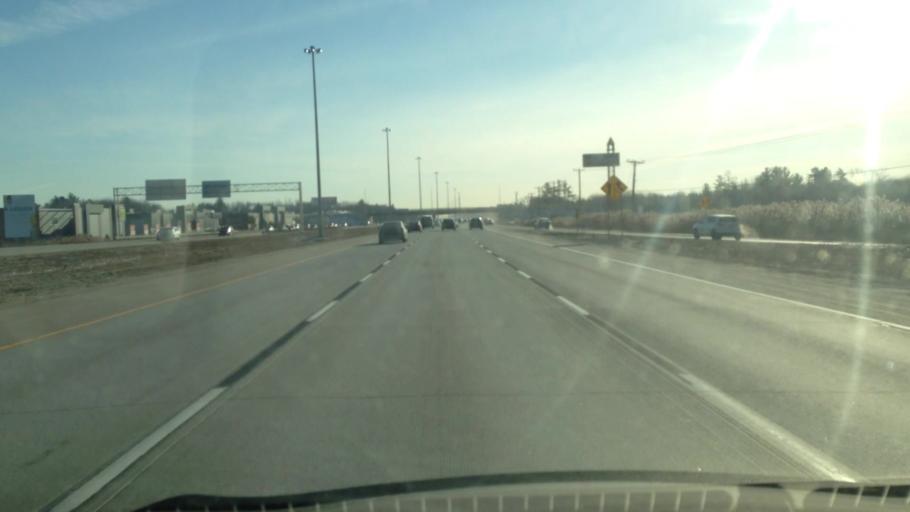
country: CA
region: Quebec
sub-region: Laurentides
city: Blainville
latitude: 45.6795
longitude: -73.9177
